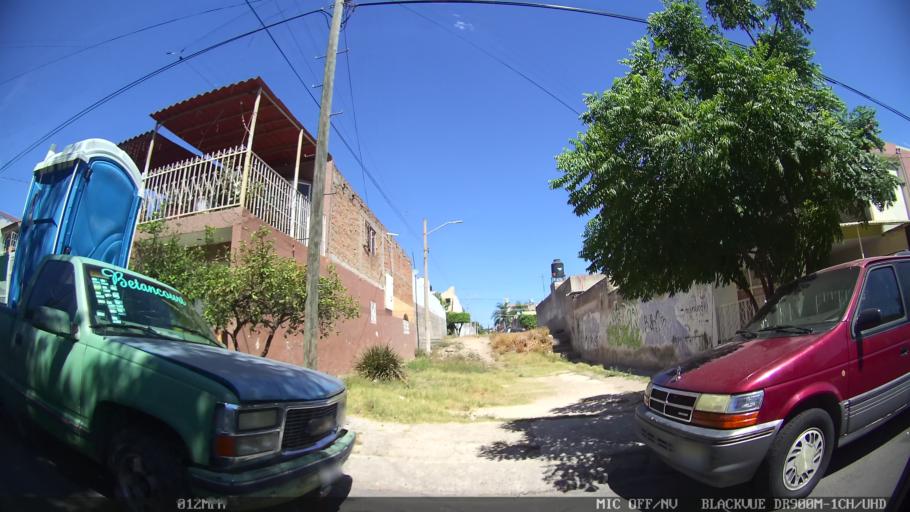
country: MX
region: Jalisco
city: Tlaquepaque
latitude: 20.6914
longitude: -103.2861
